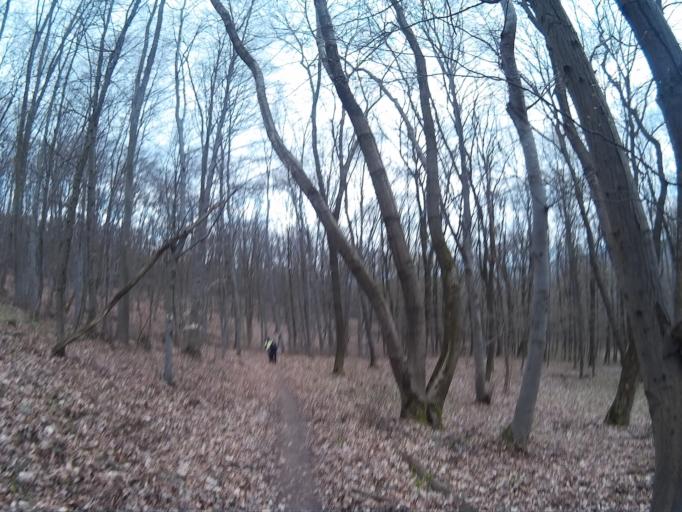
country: HU
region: Pest
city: Kosd
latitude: 47.8404
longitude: 19.1402
